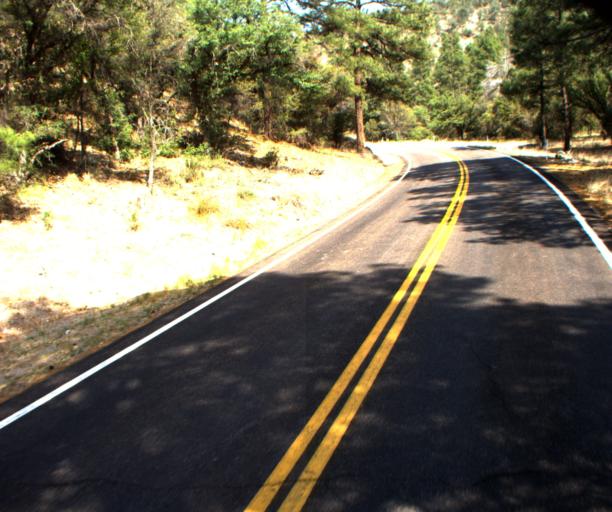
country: US
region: Arizona
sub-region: Greenlee County
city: Clifton
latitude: 33.1018
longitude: -109.0597
